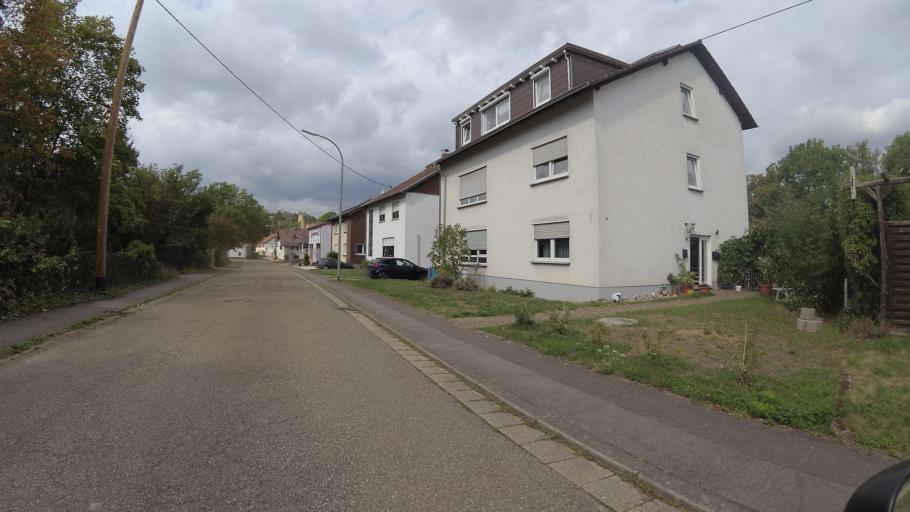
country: FR
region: Lorraine
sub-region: Departement de la Moselle
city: Sarreinsming
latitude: 49.1346
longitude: 7.1351
